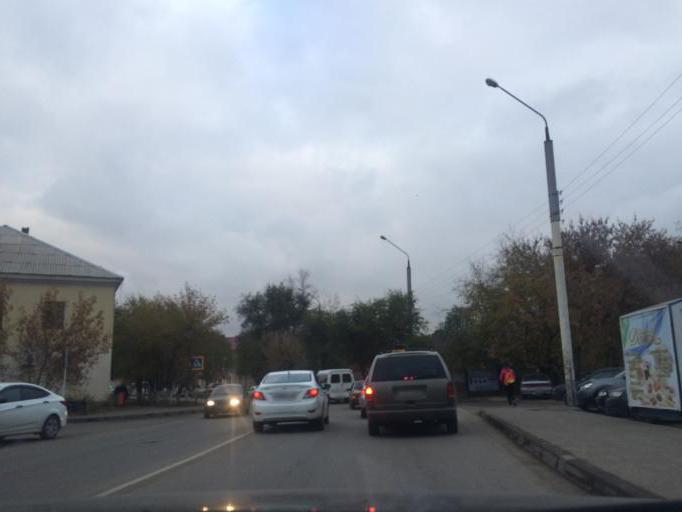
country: KZ
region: Astana Qalasy
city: Astana
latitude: 51.1930
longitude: 71.4023
